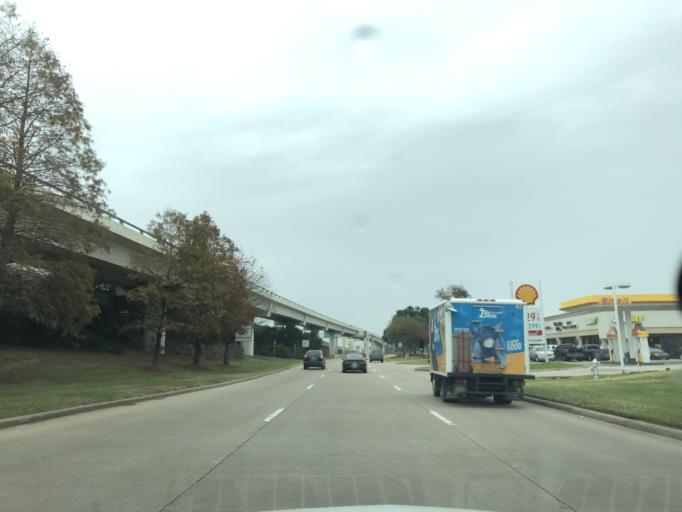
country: US
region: Texas
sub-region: Fort Bend County
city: Meadows Place
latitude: 29.6214
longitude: -95.6010
